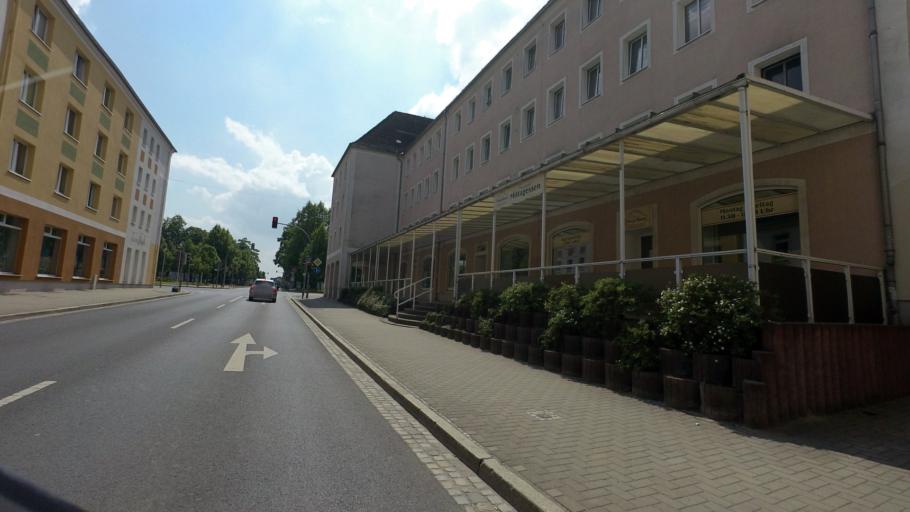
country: DE
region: Saxony
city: Niesky
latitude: 51.2940
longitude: 14.8232
